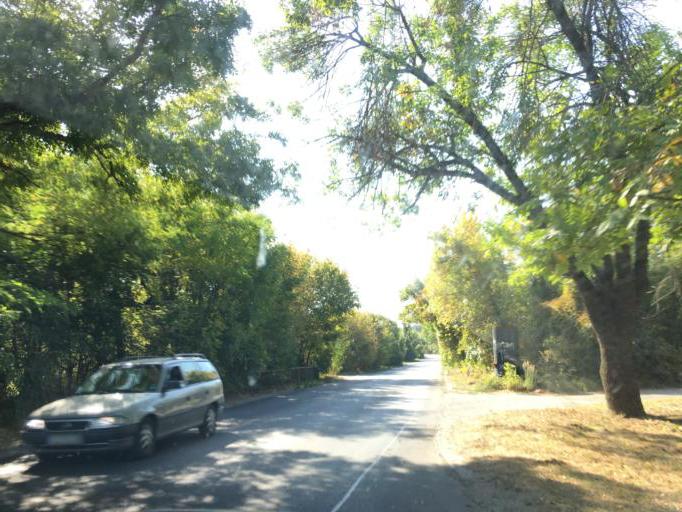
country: BG
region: Pazardzhik
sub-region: Obshtina Pazardzhik
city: Pazardzhik
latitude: 42.1219
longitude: 24.2938
